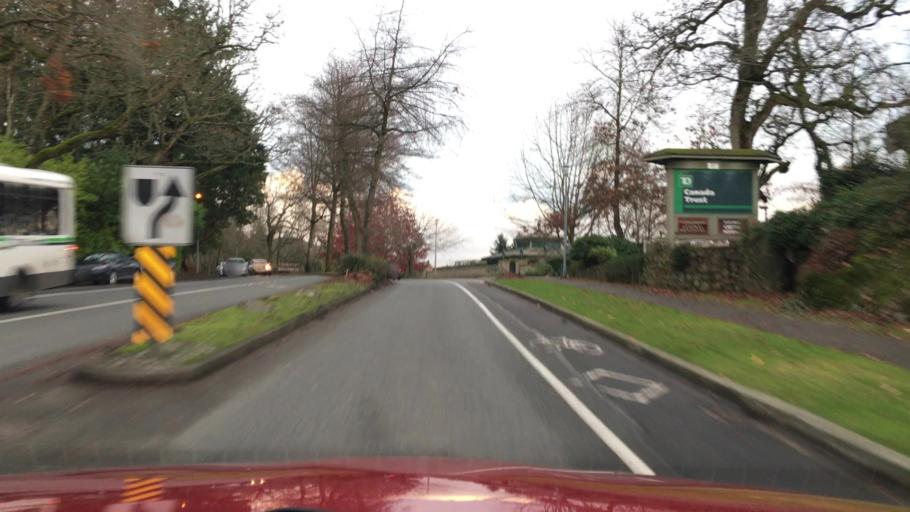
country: CA
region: British Columbia
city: Victoria
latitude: 48.4978
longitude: -123.3793
